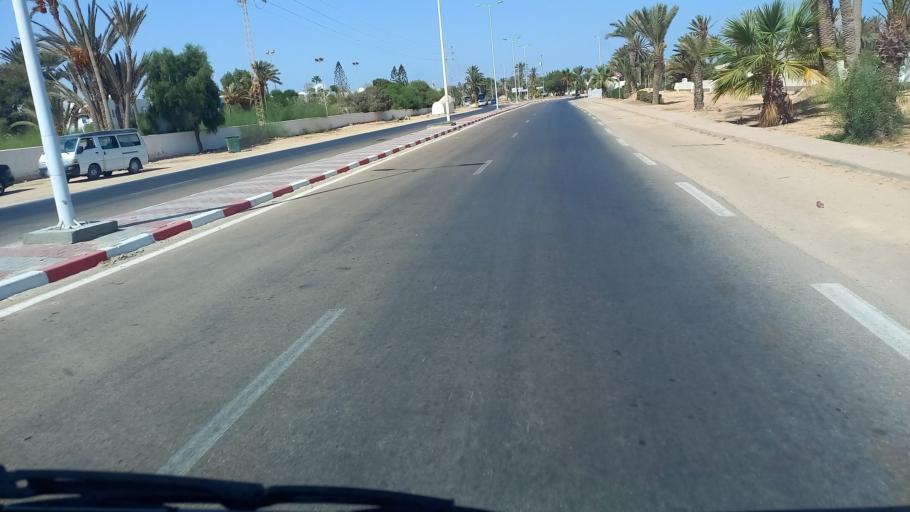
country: TN
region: Madanin
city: Midoun
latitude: 33.8268
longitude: 11.0333
